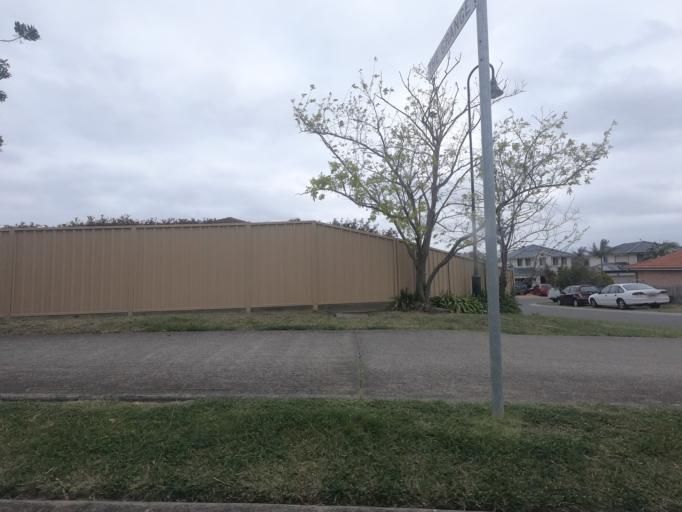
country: AU
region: New South Wales
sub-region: Wollongong
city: Dapto
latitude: -34.4876
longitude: 150.7768
